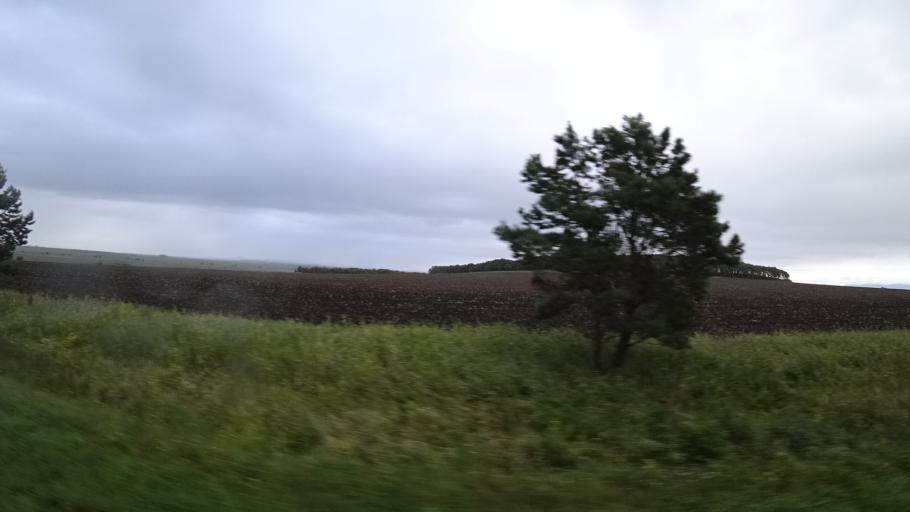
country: RU
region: Primorskiy
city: Chernigovka
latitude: 44.3694
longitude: 132.5319
